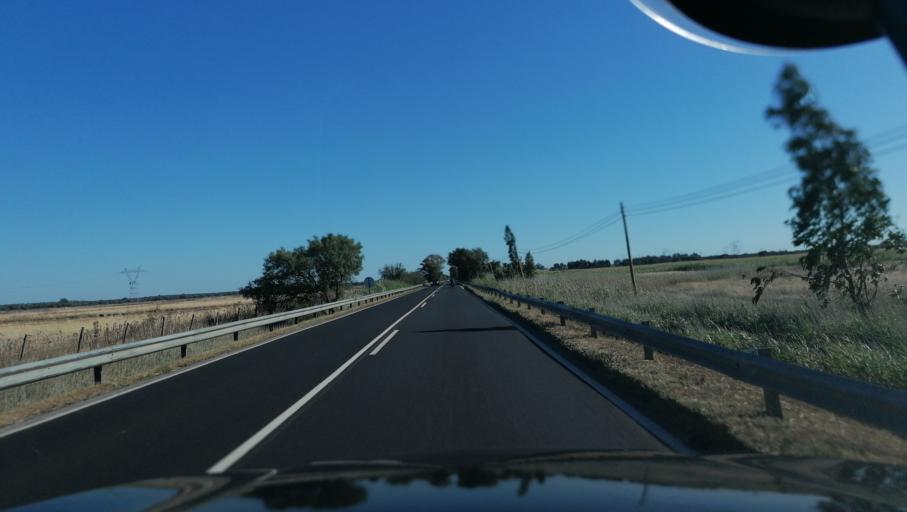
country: PT
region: Santarem
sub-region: Benavente
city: Samora Correia
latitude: 38.8800
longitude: -8.8813
